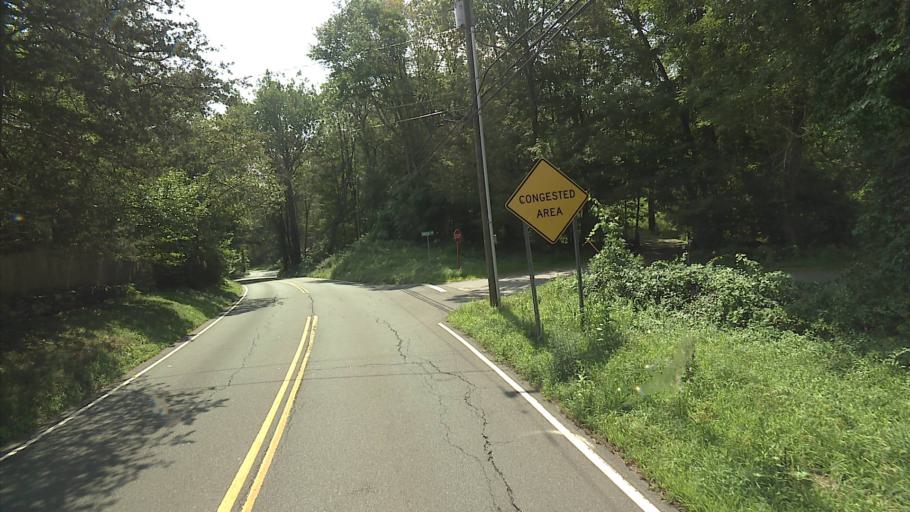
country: US
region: Connecticut
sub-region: Middlesex County
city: East Haddam
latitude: 41.4585
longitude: -72.4578
